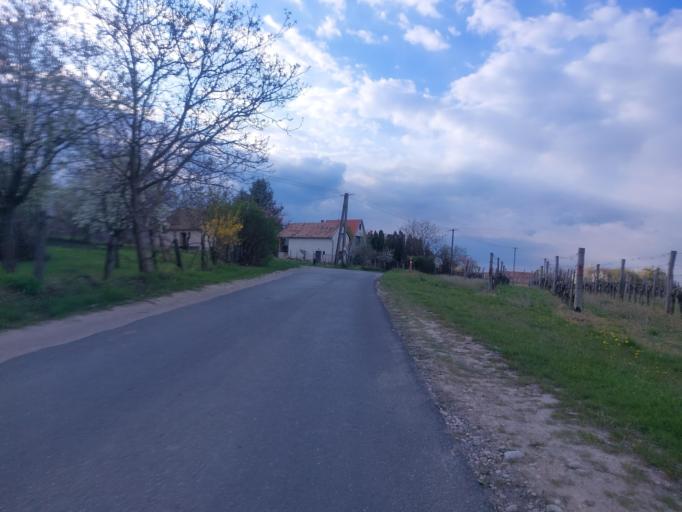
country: HU
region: Veszprem
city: Devecser
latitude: 47.1491
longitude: 17.3852
